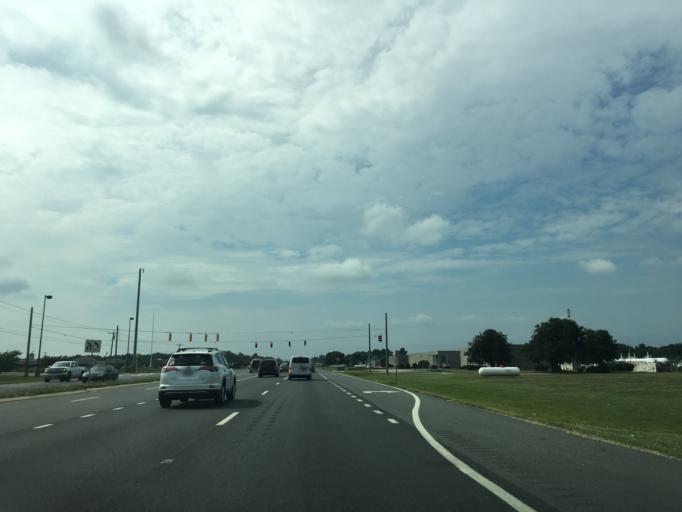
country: US
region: Delaware
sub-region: Sussex County
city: Millsboro
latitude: 38.5710
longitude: -75.2823
